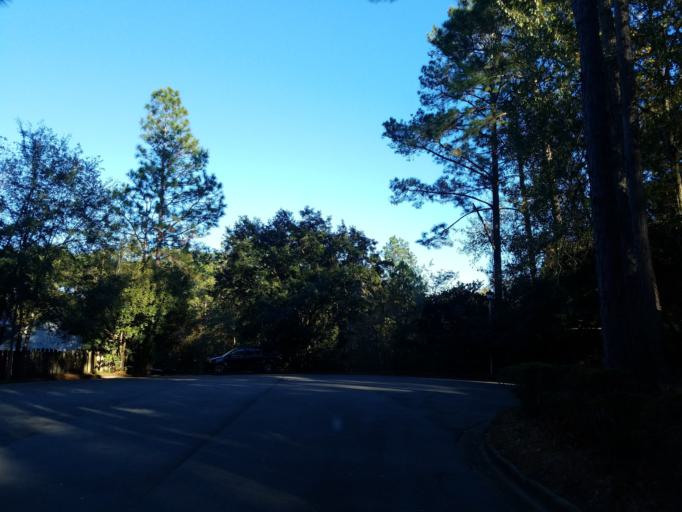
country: US
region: Mississippi
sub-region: Lamar County
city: West Hattiesburg
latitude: 31.3089
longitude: -89.3488
